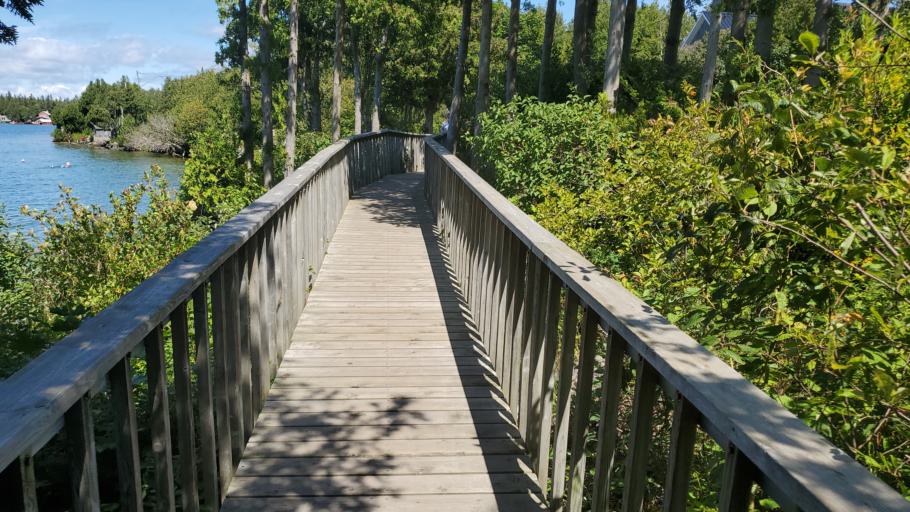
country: CA
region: Ontario
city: Tobermory
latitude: 45.2576
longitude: -81.6610
